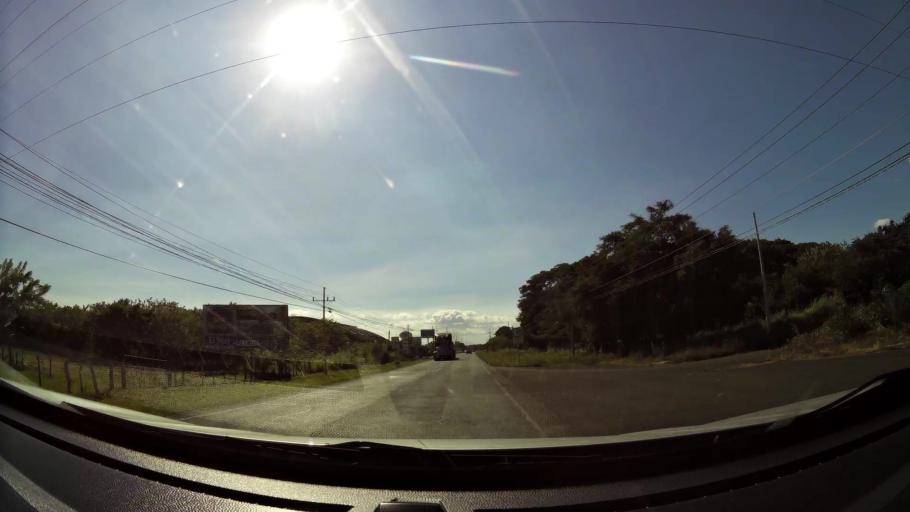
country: CR
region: Guanacaste
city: Liberia
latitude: 10.6182
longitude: -85.4641
